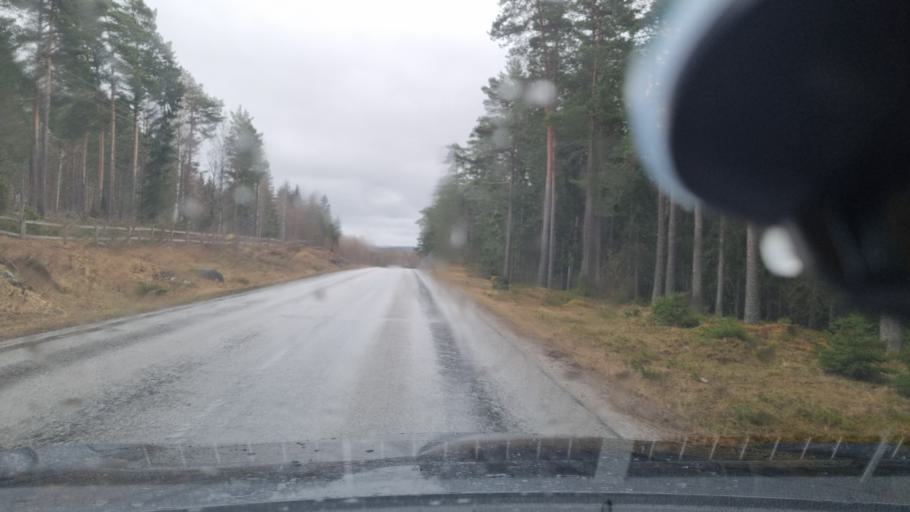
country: SE
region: Stockholm
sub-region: Sigtuna Kommun
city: Sigtuna
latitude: 59.5543
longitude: 17.7264
